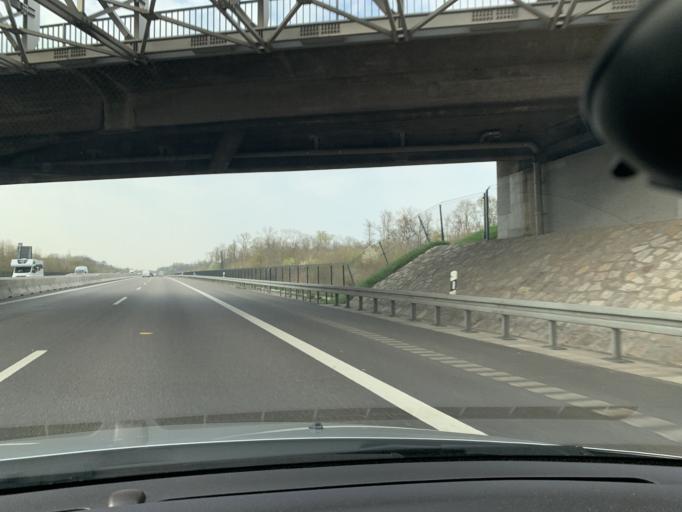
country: DE
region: Baden-Wuerttemberg
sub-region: Freiburg Region
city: Mahlberg
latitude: 48.3218
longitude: 7.7904
